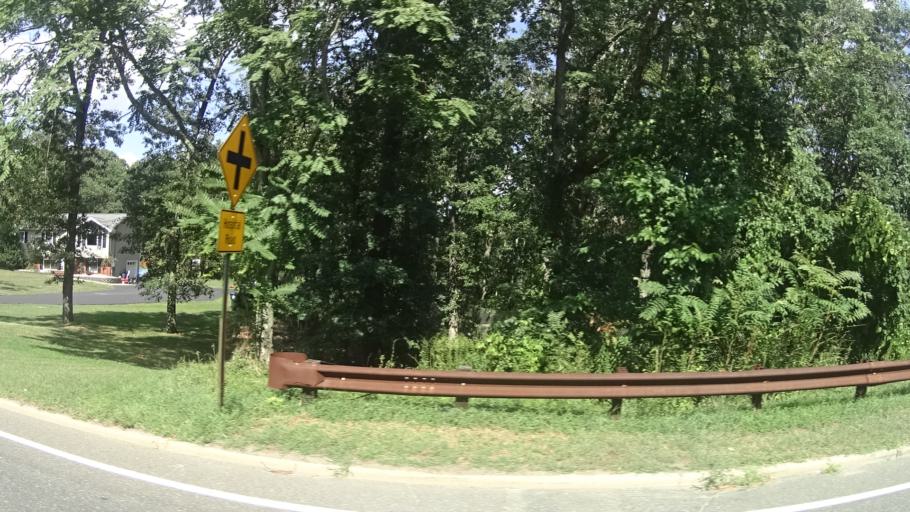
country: US
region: New Jersey
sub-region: Monmouth County
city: Ramtown
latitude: 40.1505
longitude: -74.1078
